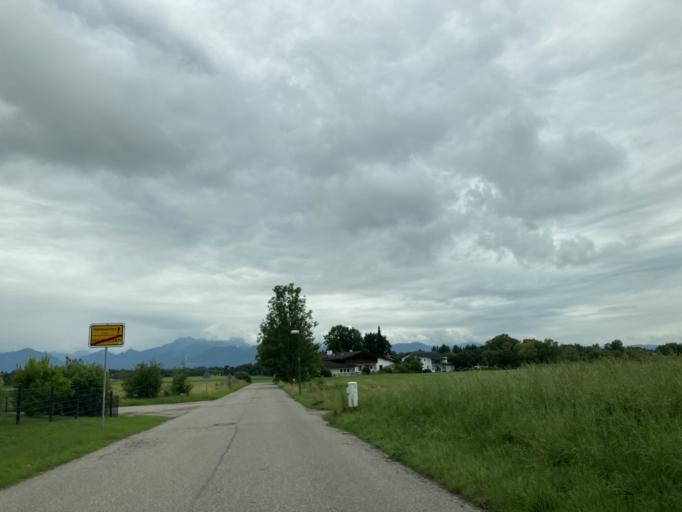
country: DE
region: Bavaria
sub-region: Upper Bavaria
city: Stephanskirchen
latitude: 47.8581
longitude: 12.1788
